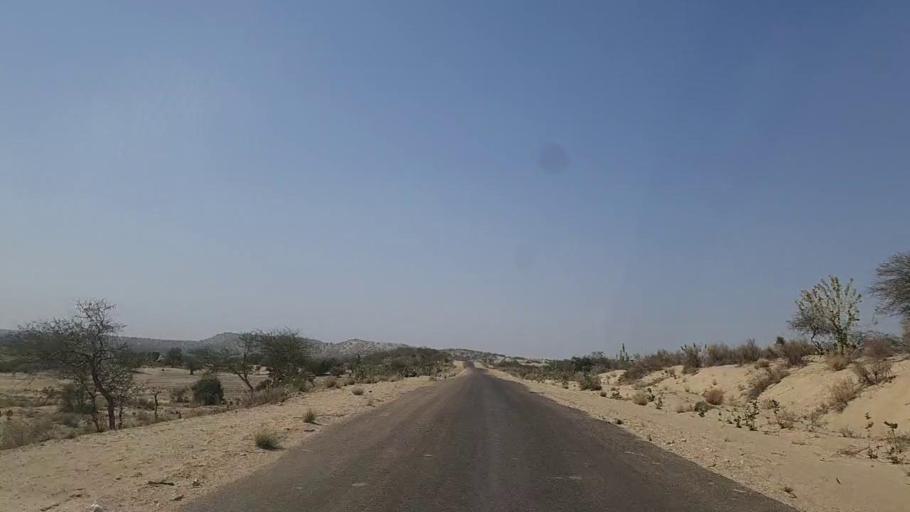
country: PK
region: Sindh
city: Diplo
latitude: 24.5643
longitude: 69.4640
